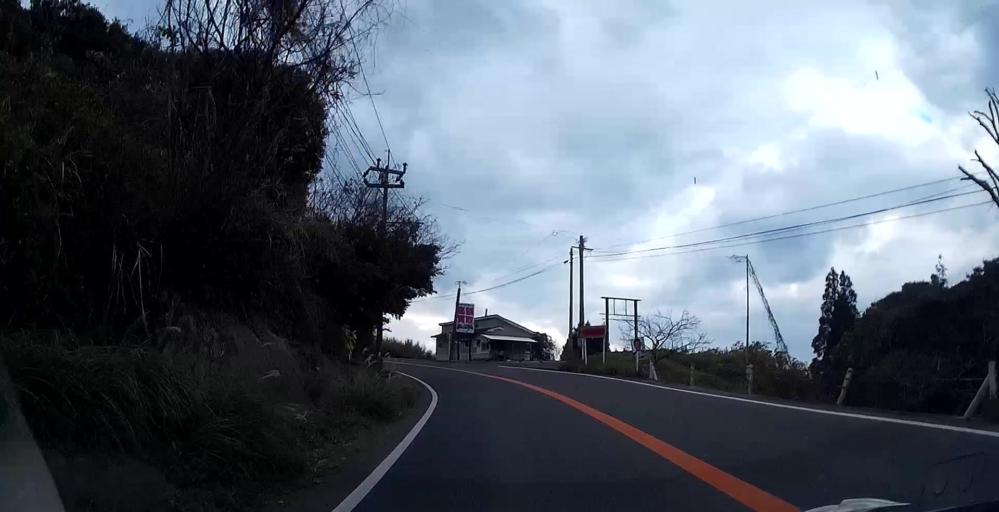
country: JP
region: Kagoshima
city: Akune
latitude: 32.1001
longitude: 130.1765
